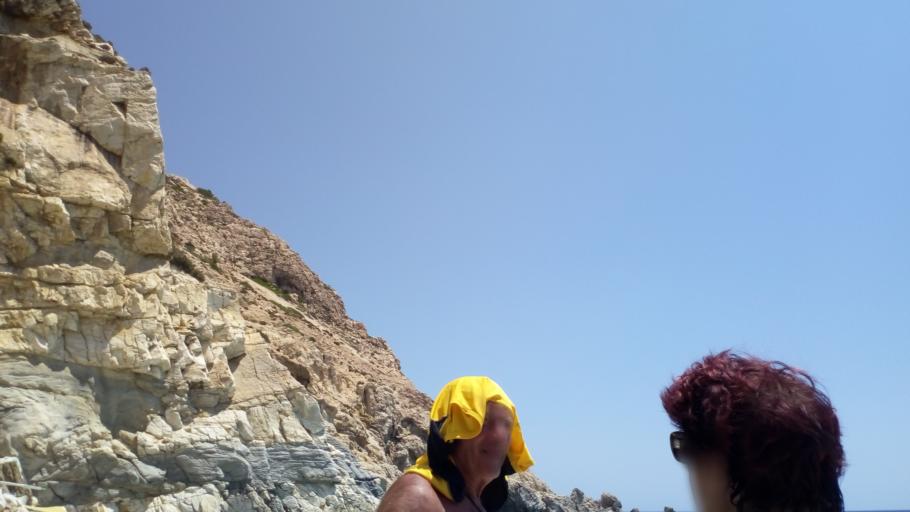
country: GR
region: North Aegean
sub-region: Nomos Samou
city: Agios Kirykos
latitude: 37.5593
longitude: 26.1405
